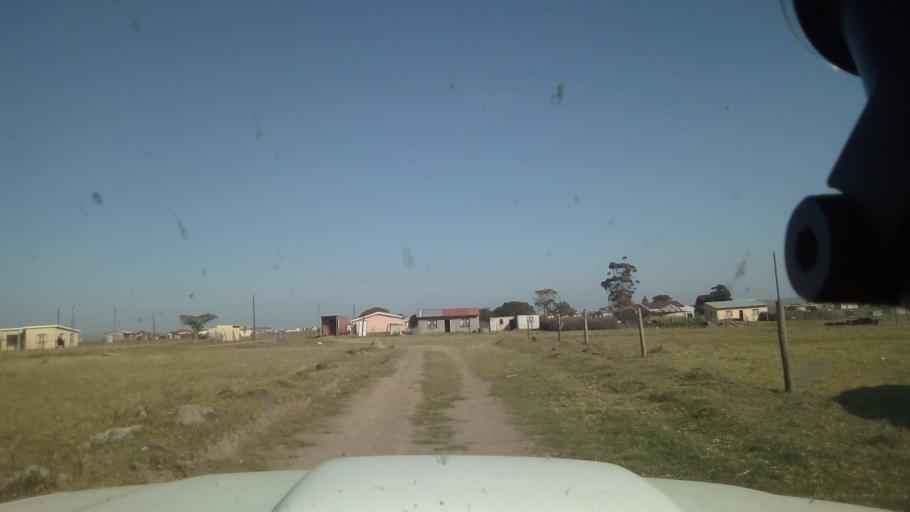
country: ZA
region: Eastern Cape
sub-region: Buffalo City Metropolitan Municipality
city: Bhisho
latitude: -32.9392
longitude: 27.3369
